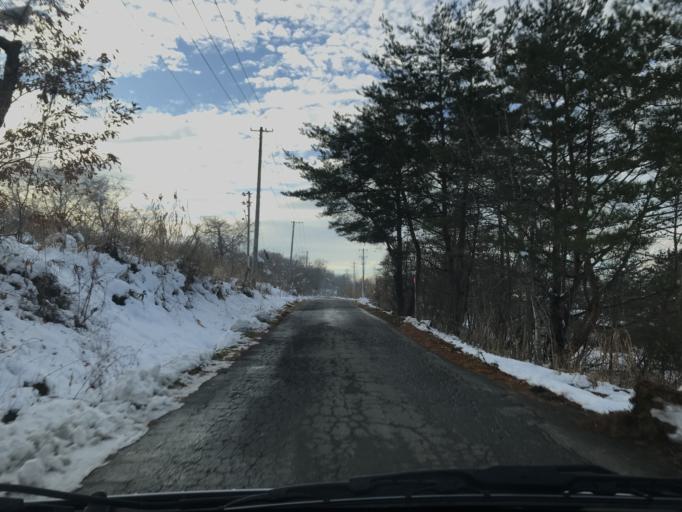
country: JP
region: Iwate
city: Mizusawa
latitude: 39.0523
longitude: 141.0761
